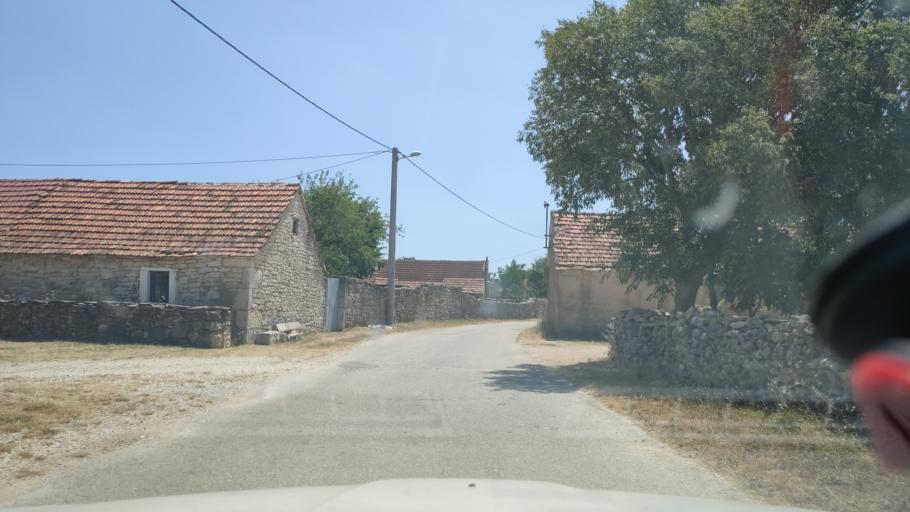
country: HR
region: Sibensko-Kniniska
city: Kistanje
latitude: 43.9554
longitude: 15.8797
